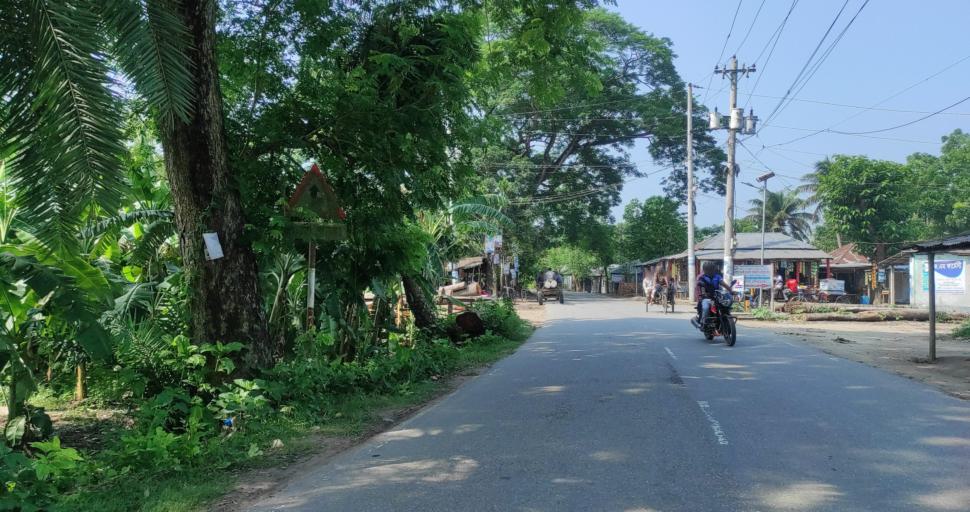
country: BD
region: Rajshahi
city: Ishurdi
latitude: 24.2871
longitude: 89.0656
